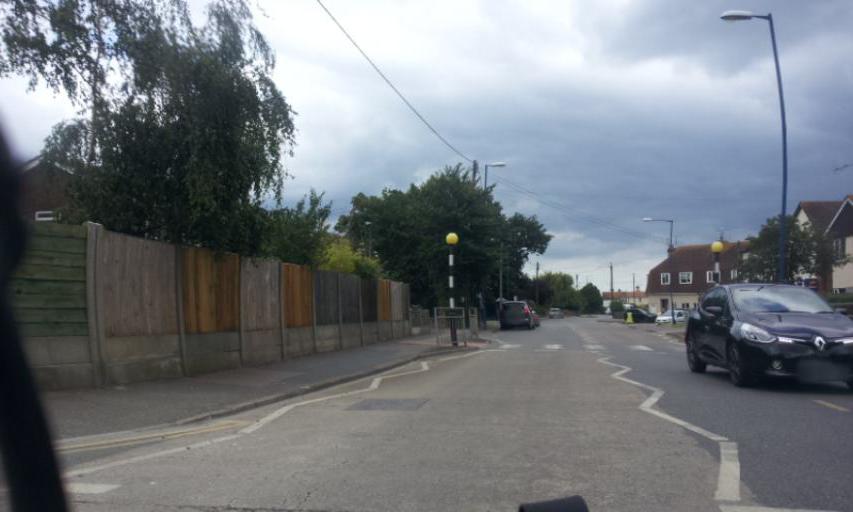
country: GB
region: England
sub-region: Kent
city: Tankerton
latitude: 51.3611
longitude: 1.0675
